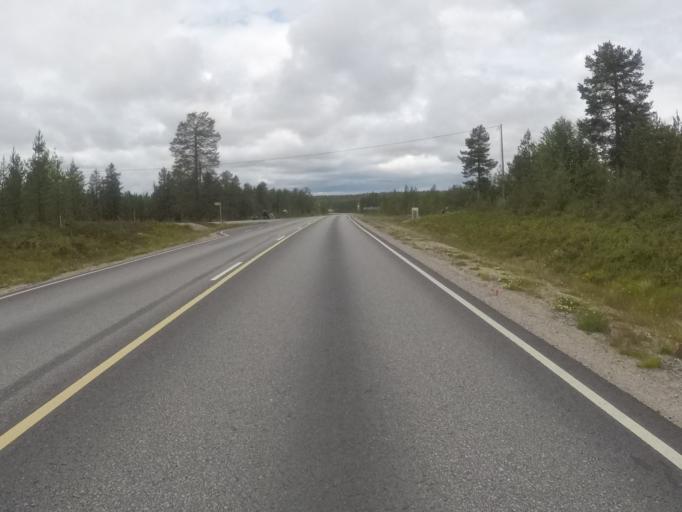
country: FI
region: Lapland
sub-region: Tunturi-Lappi
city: Muonio
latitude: 67.9852
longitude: 23.6470
